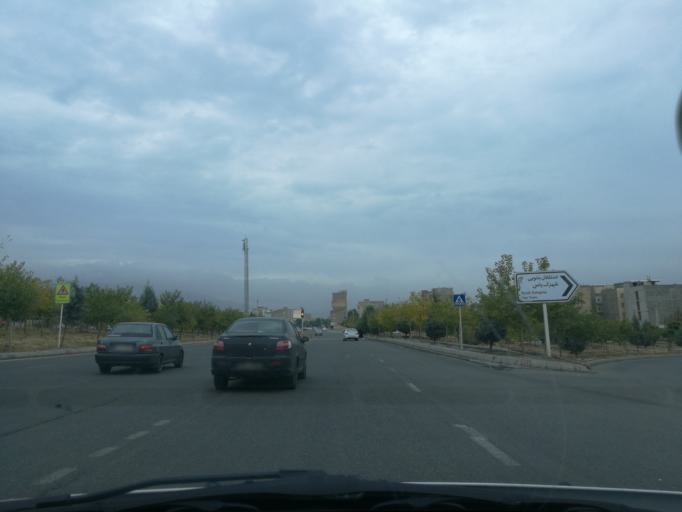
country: IR
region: Alborz
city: Karaj
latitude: 35.8628
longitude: 50.9328
